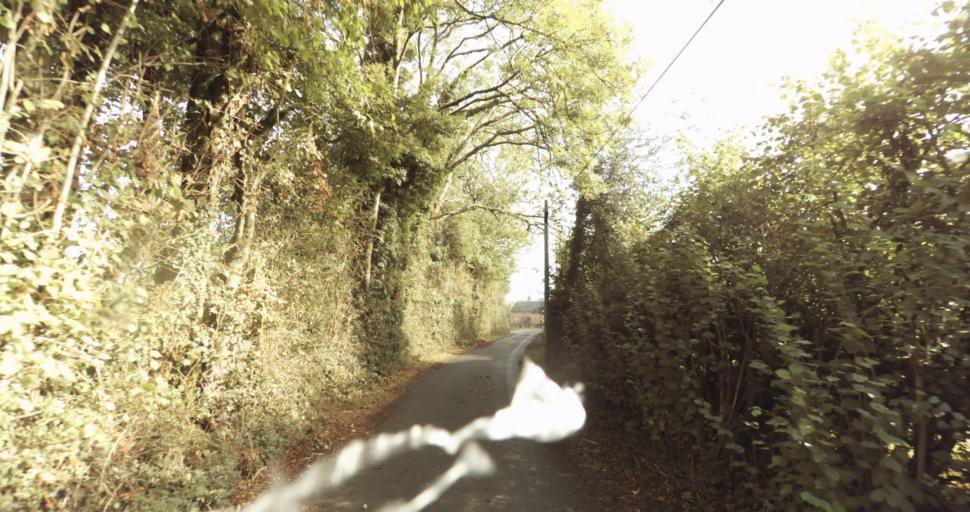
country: FR
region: Lower Normandy
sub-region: Departement de l'Orne
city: Gace
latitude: 48.8544
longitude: 0.2956
